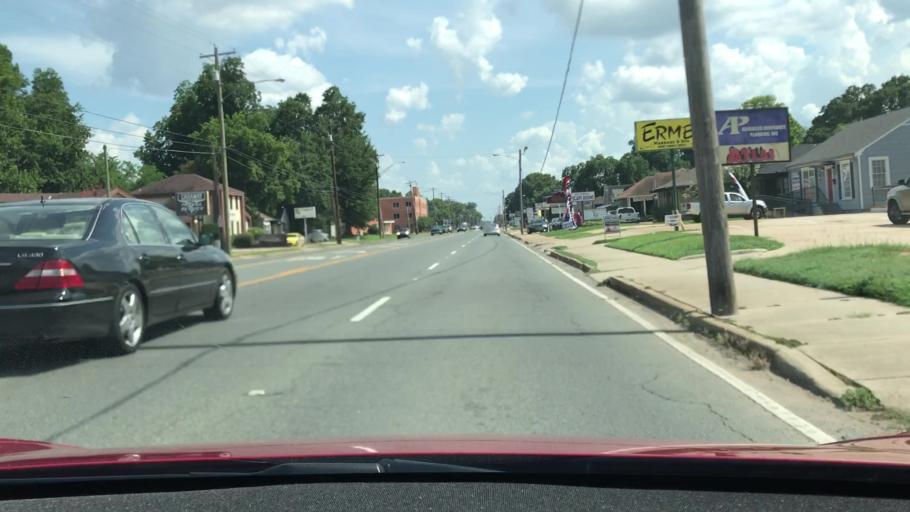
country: US
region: Louisiana
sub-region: Bossier Parish
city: Bossier City
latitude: 32.4744
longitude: -93.7223
